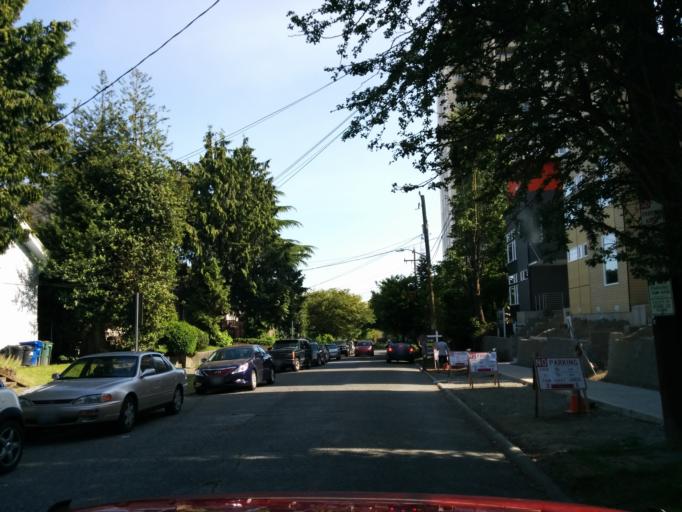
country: US
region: Washington
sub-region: King County
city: Seattle
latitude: 47.6639
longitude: -122.3185
